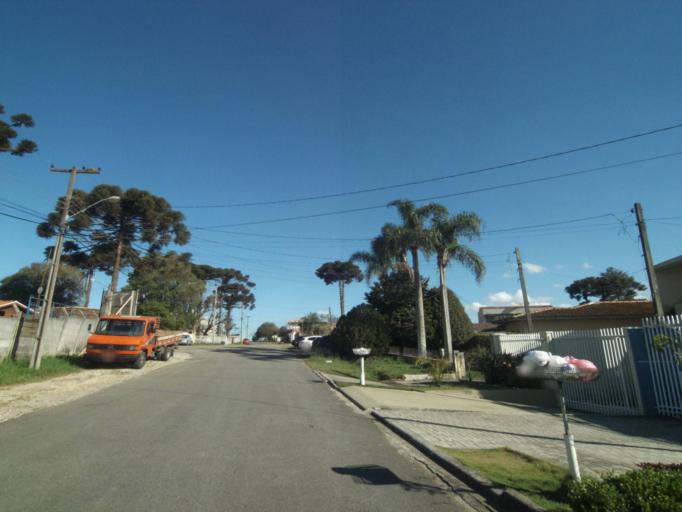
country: BR
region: Parana
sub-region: Curitiba
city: Curitiba
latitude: -25.3891
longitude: -49.2570
